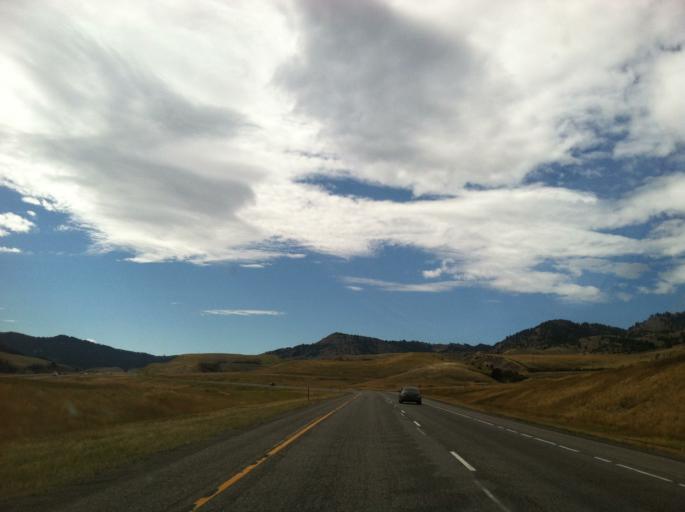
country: US
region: Montana
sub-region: Park County
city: Livingston
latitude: 45.6638
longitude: -110.7157
